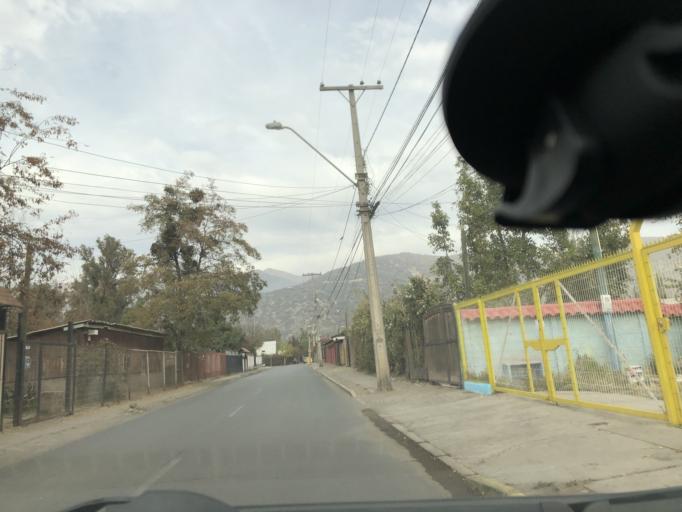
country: CL
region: Santiago Metropolitan
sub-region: Provincia de Cordillera
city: Puente Alto
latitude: -33.6069
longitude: -70.5177
